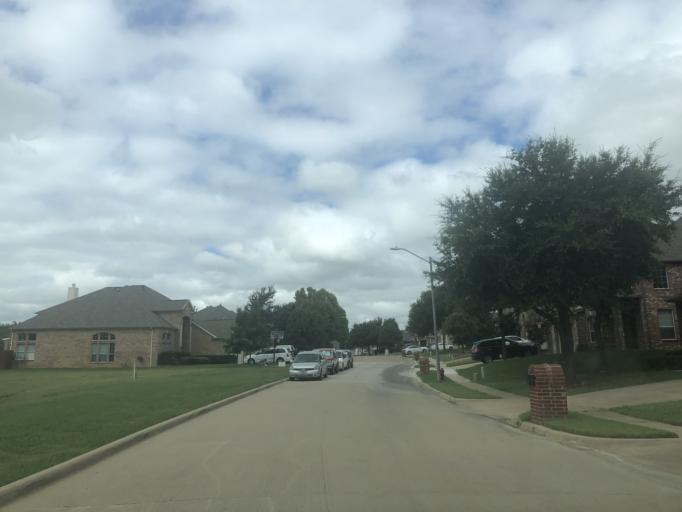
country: US
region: Texas
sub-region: Dallas County
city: Cedar Hill
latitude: 32.6540
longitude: -96.9964
